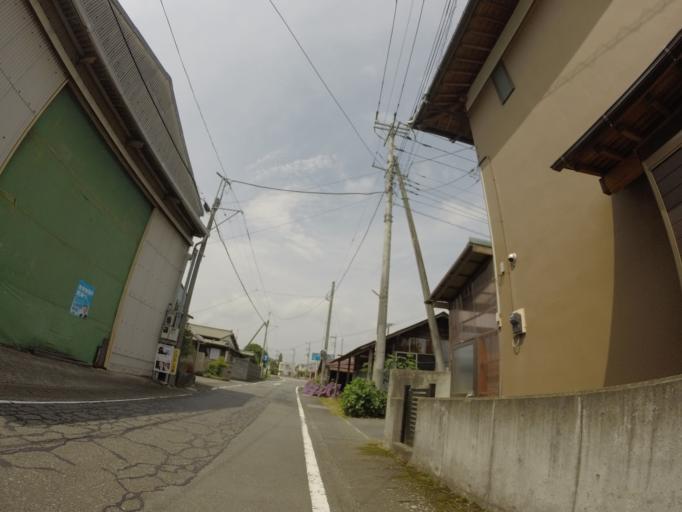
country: JP
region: Shizuoka
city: Fujinomiya
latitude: 35.3036
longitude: 138.5940
